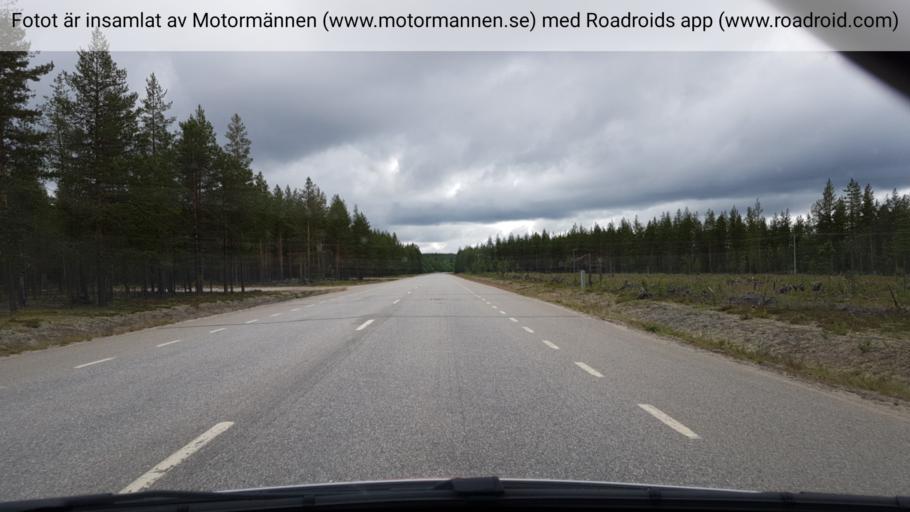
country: SE
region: Vaesterbotten
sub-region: Norsjo Kommun
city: Norsjoe
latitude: 64.6018
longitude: 19.2982
